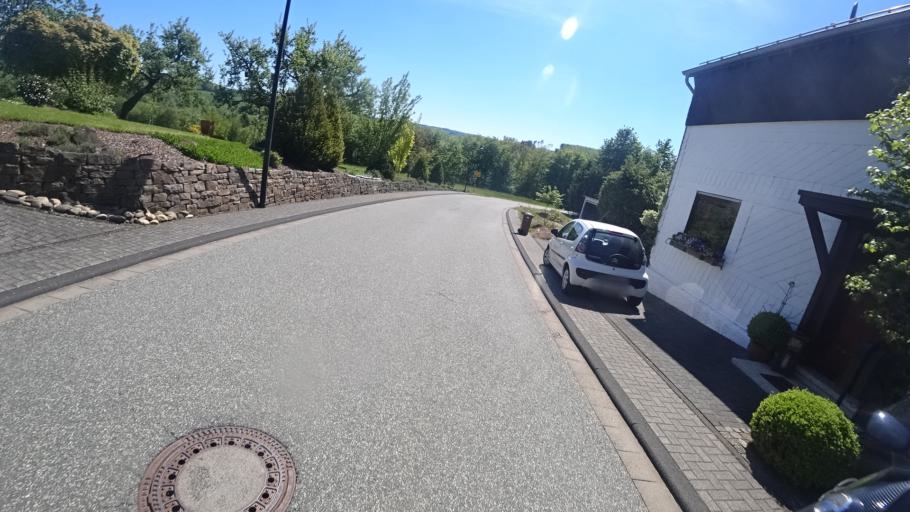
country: DE
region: Rheinland-Pfalz
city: Steineroth
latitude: 50.7480
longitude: 7.8564
